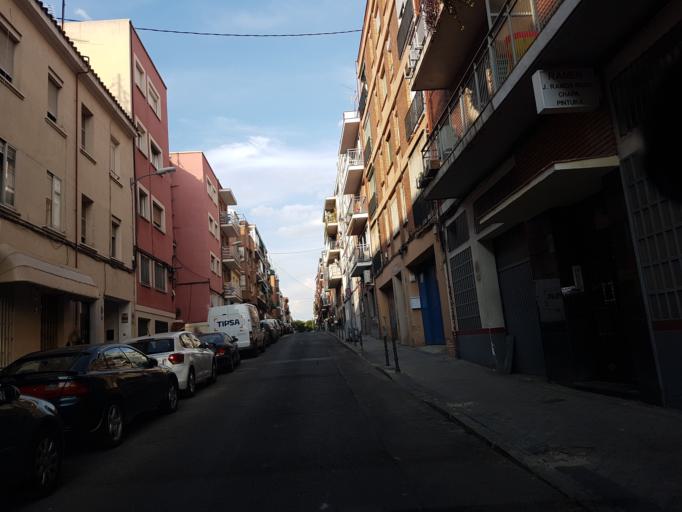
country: ES
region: Madrid
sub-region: Provincia de Madrid
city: Ciudad Lineal
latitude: 40.4378
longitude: -3.6441
